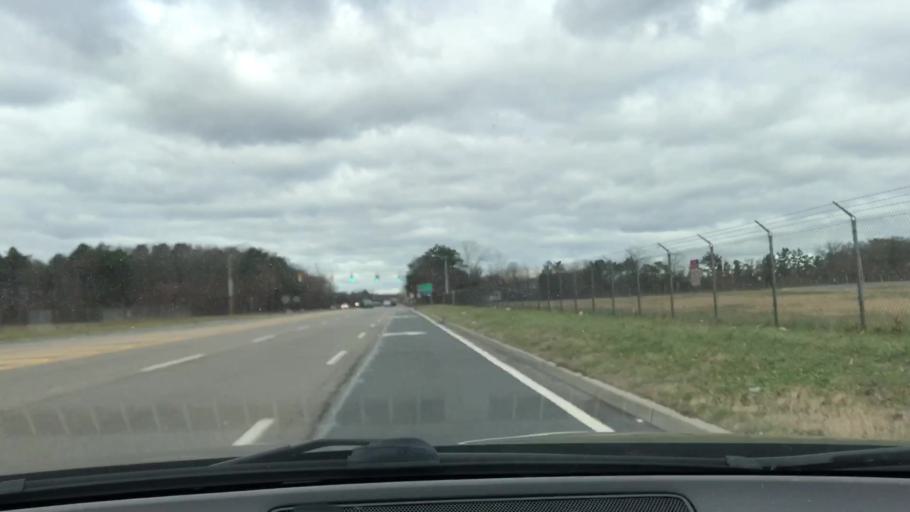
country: US
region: New York
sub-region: Suffolk County
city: Bohemia
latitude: 40.7875
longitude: -73.1153
